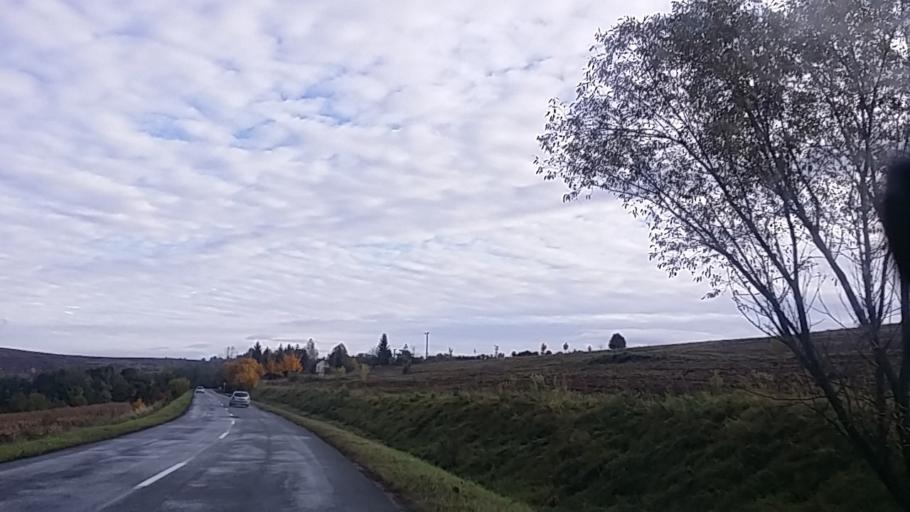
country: HU
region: Heves
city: Szilvasvarad
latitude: 48.1345
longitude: 20.4180
